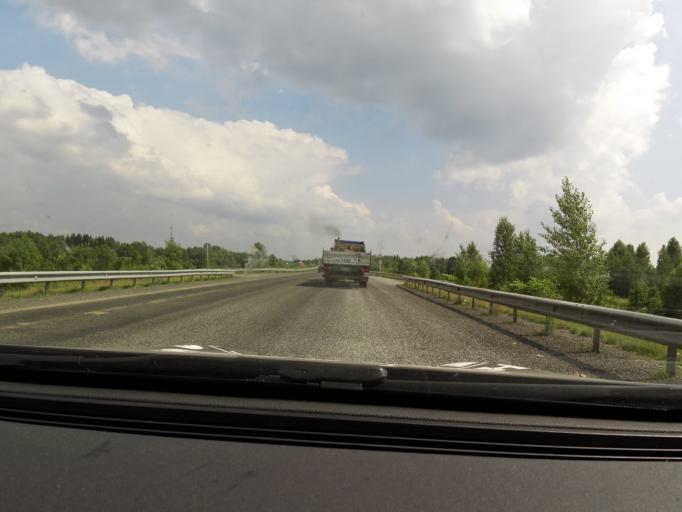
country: RU
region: Sverdlovsk
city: Ufimskiy
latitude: 56.7659
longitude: 58.1356
